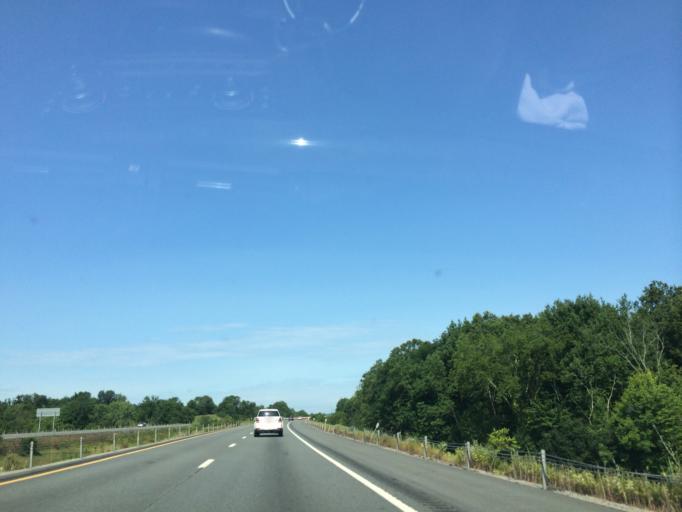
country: US
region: New York
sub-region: Orange County
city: Orange Lake
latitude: 41.5127
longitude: -74.1498
